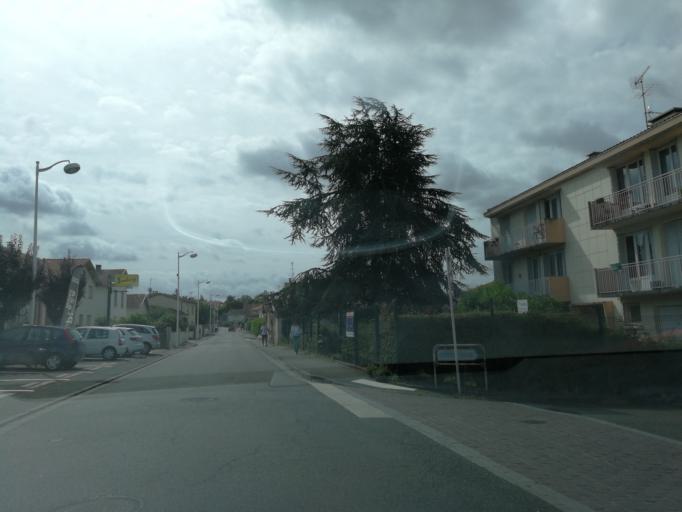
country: FR
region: Midi-Pyrenees
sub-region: Departement de la Haute-Garonne
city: Balma
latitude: 43.6116
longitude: 1.4952
